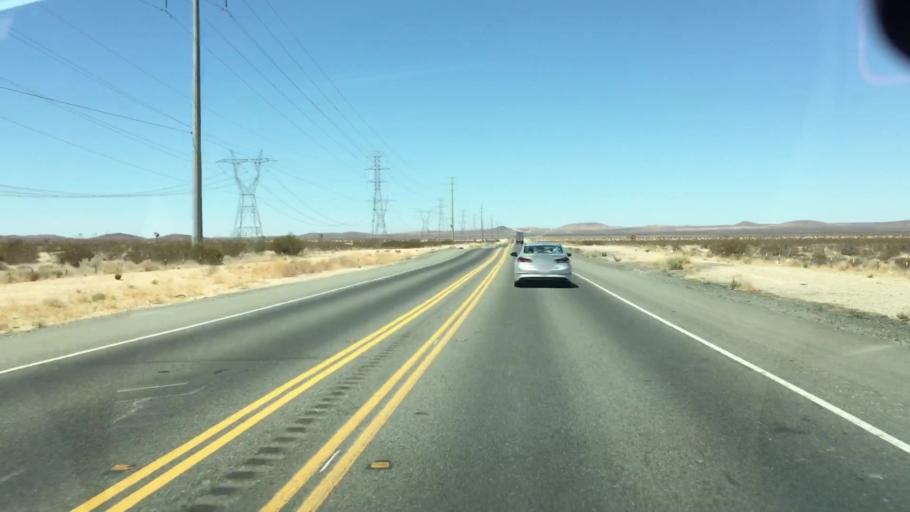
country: US
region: California
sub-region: San Bernardino County
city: Adelanto
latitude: 34.7820
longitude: -117.4812
